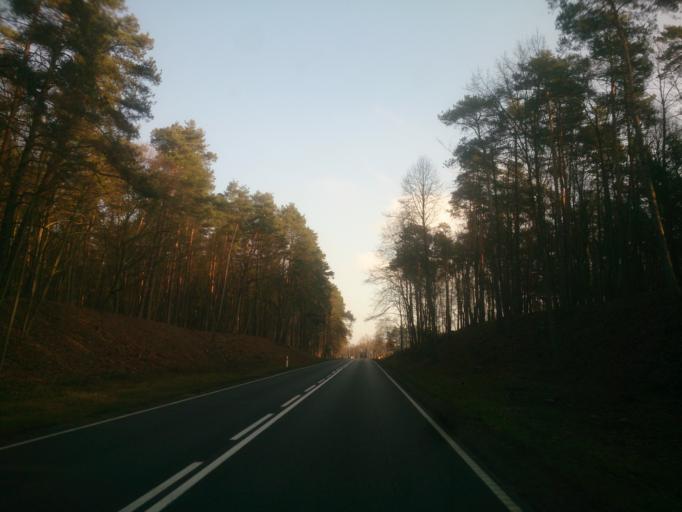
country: PL
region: Kujawsko-Pomorskie
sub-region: Powiat brodnicki
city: Brodnica
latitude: 53.2844
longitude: 19.4836
